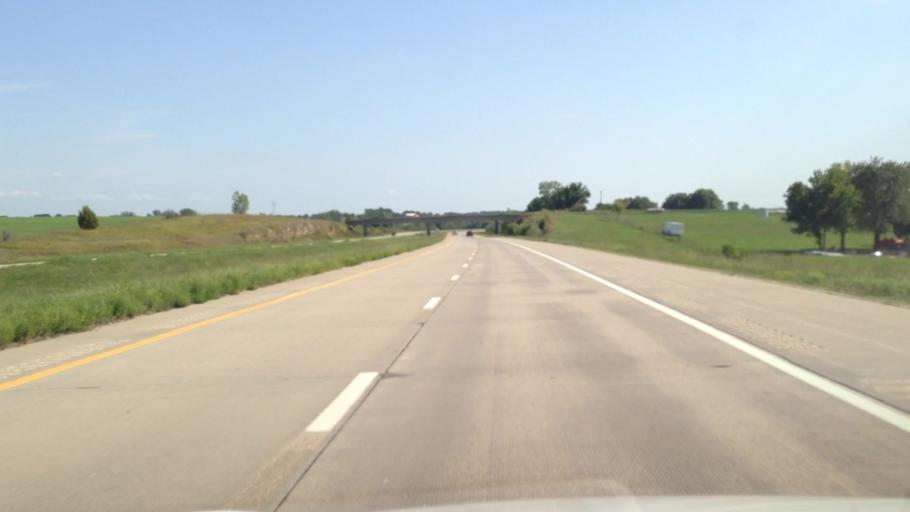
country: US
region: Kansas
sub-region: Miami County
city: Louisburg
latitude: 38.5520
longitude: -94.6896
